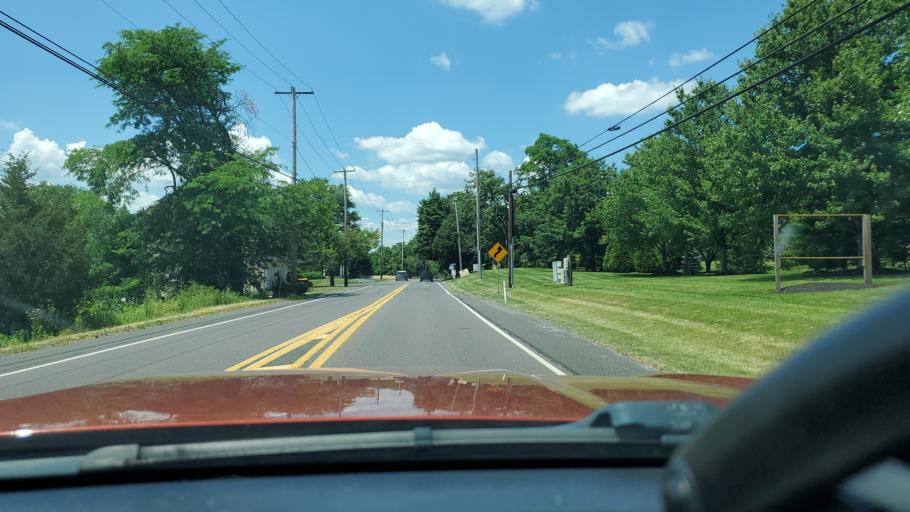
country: US
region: Pennsylvania
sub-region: Montgomery County
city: Limerick
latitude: 40.3026
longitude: -75.5290
